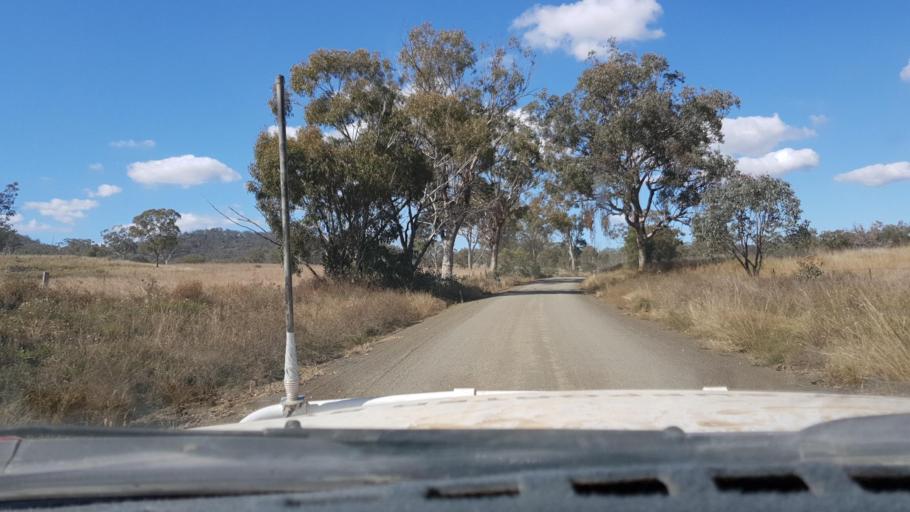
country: AU
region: New South Wales
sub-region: Tamworth Municipality
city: Manilla
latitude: -30.4710
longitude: 150.7526
